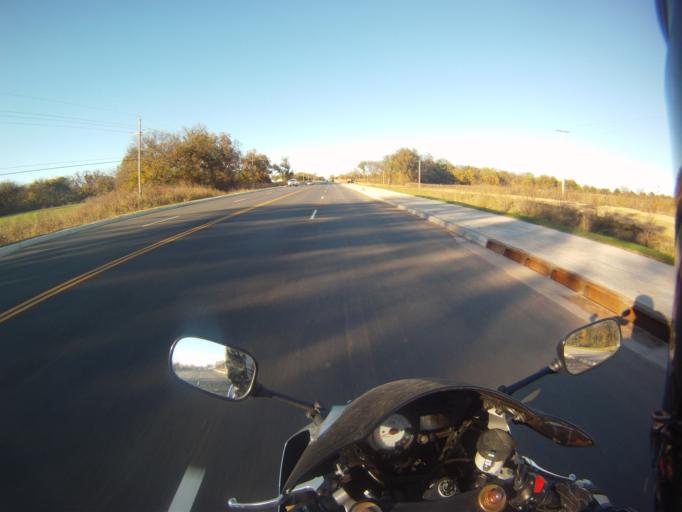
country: US
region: Oklahoma
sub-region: Payne County
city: Stillwater
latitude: 36.1246
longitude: -97.1232
